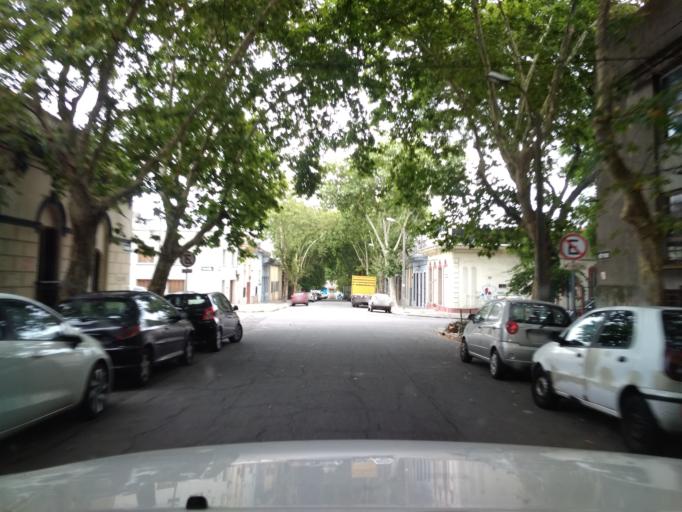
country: UY
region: Montevideo
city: Montevideo
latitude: -34.8966
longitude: -56.1855
